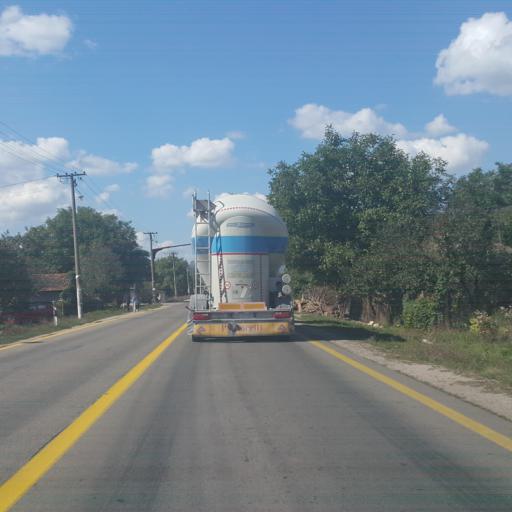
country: RS
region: Central Serbia
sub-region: Pirotski Okrug
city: Bela Palanka
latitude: 43.2656
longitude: 22.2495
